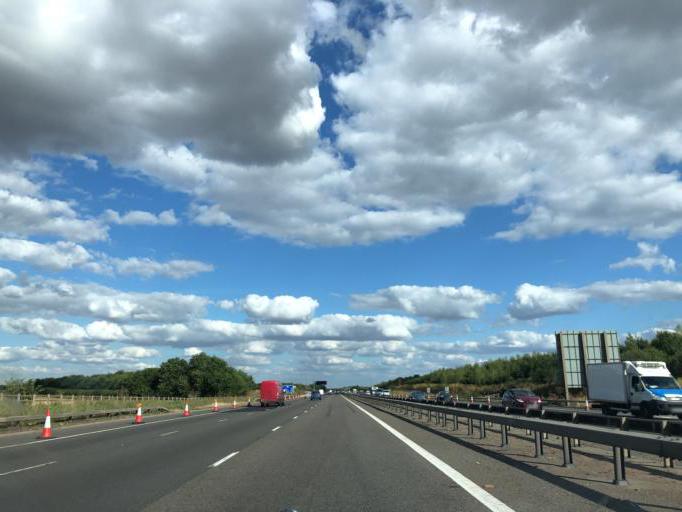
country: GB
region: England
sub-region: Milton Keynes
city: Broughton
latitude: 52.0566
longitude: -0.6944
